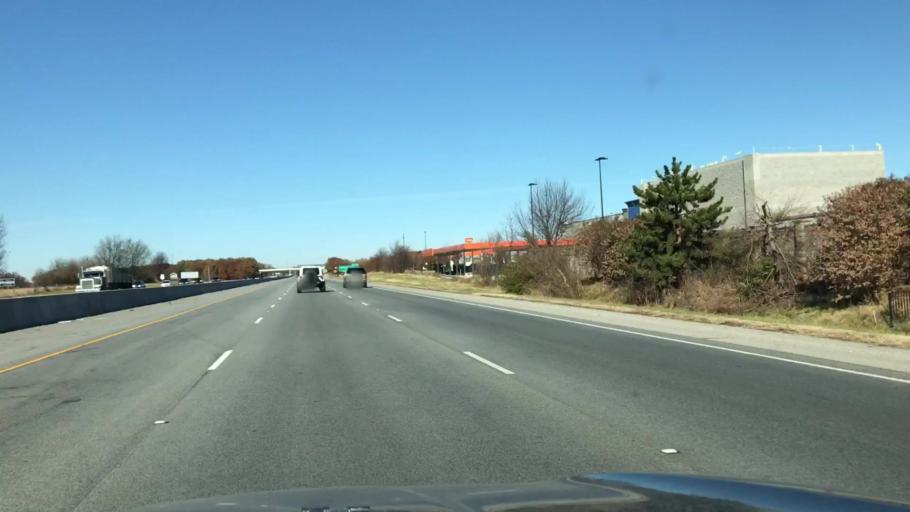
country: US
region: Arkansas
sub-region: Benton County
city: Lowell
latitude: 36.2779
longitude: -94.1518
